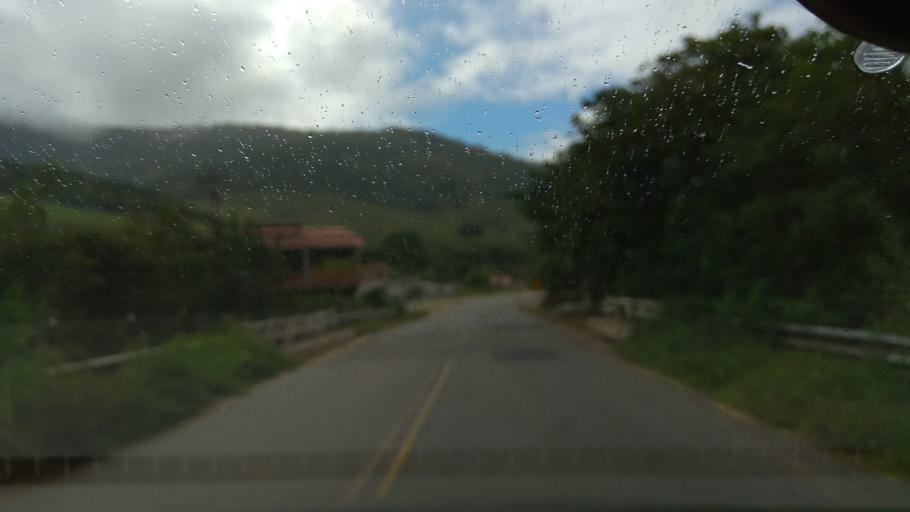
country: BR
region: Bahia
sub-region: Ubaira
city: Ubaira
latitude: -13.2512
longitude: -39.7169
